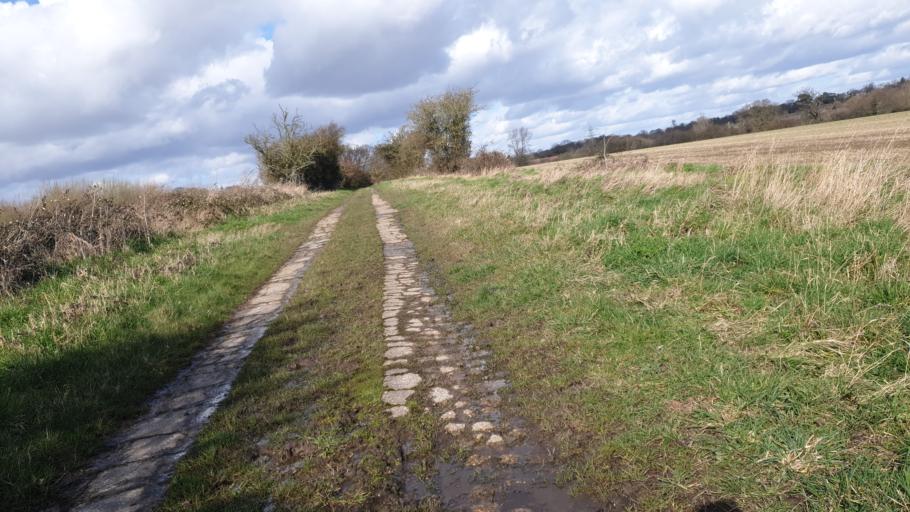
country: GB
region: England
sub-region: Essex
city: Little Clacton
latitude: 51.8425
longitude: 1.1637
